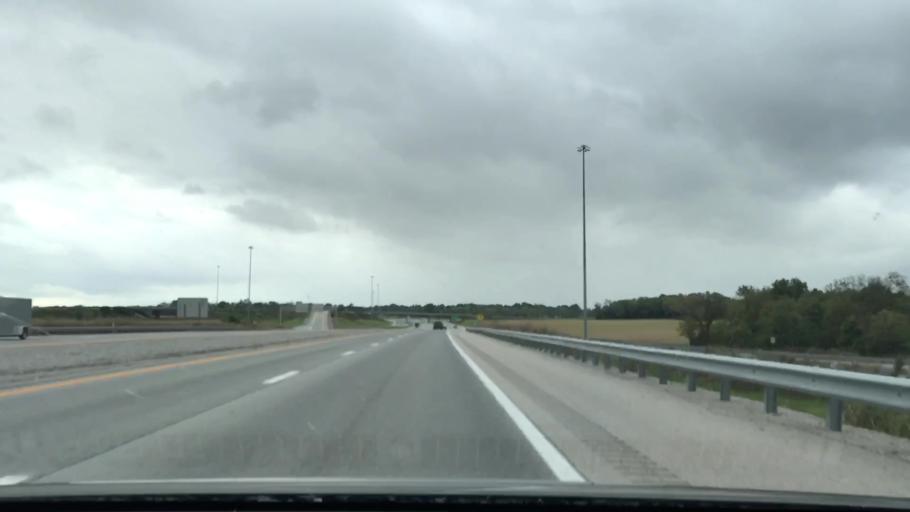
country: US
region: Kentucky
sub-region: Christian County
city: Hopkinsville
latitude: 36.8170
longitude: -87.4837
